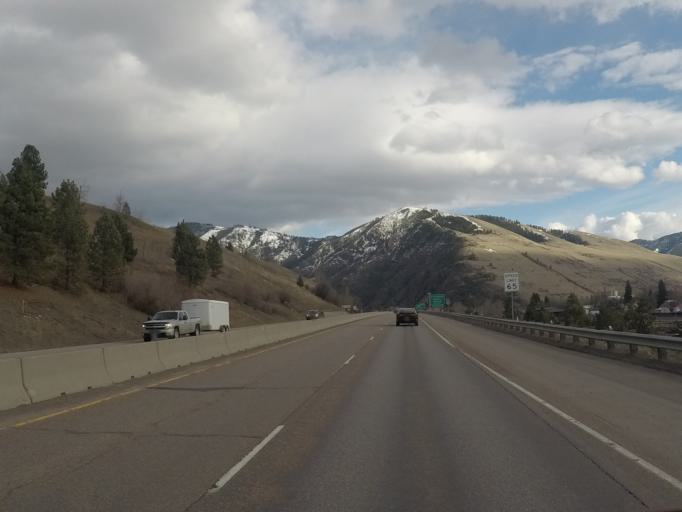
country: US
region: Montana
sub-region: Missoula County
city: Missoula
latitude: 46.8765
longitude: -113.9888
